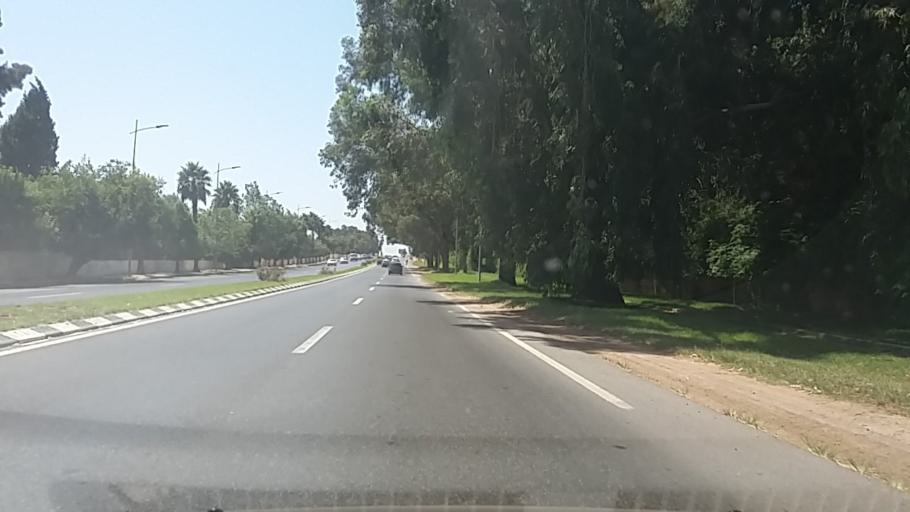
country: MA
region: Rabat-Sale-Zemmour-Zaer
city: Sale
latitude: 34.0302
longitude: -6.7469
